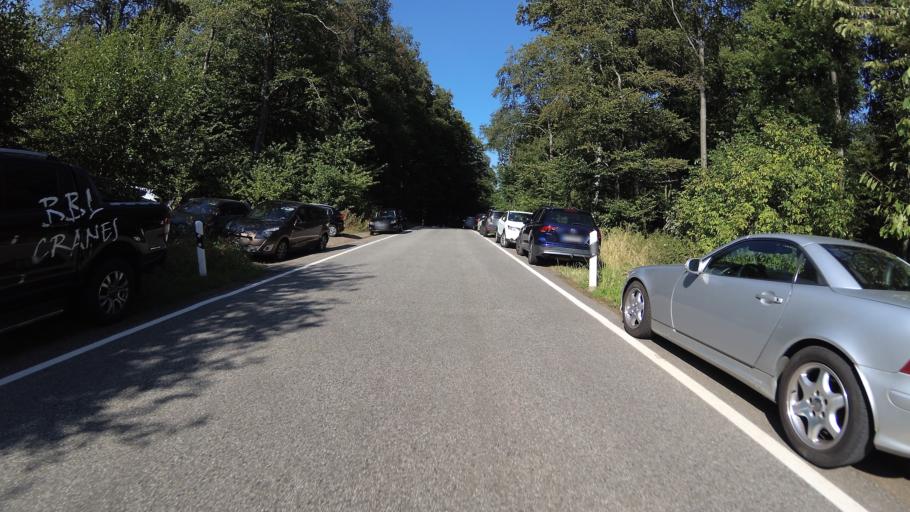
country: DE
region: Saarland
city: Eppelborn
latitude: 49.3858
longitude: 6.9538
